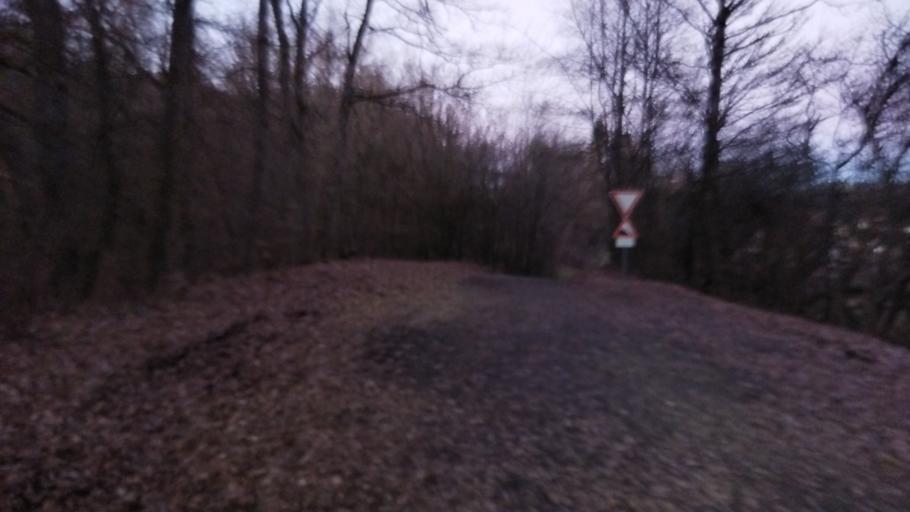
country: DE
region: Rheinland-Pfalz
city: Nanzdietschweiler
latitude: 49.4425
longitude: 7.4370
